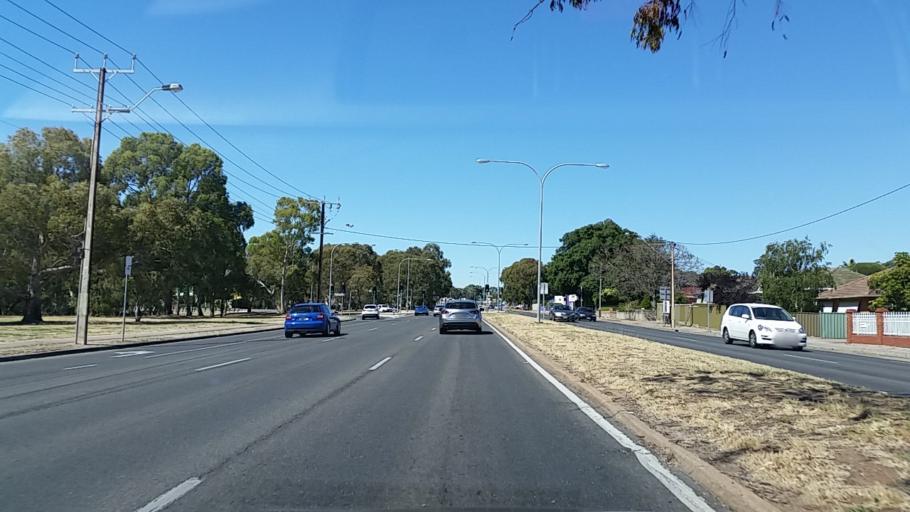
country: AU
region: South Australia
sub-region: Tea Tree Gully
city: Modbury
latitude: -34.8365
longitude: 138.6797
